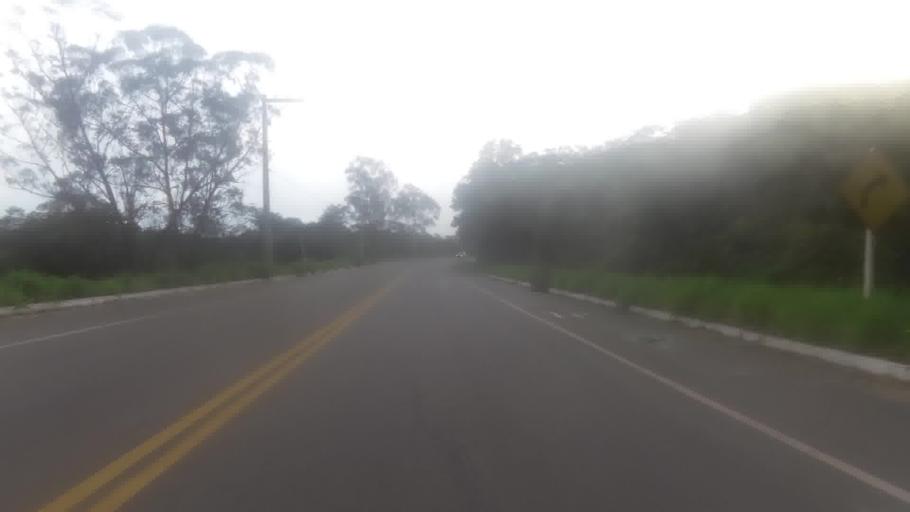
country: BR
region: Espirito Santo
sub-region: Piuma
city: Piuma
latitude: -20.8000
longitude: -40.6266
